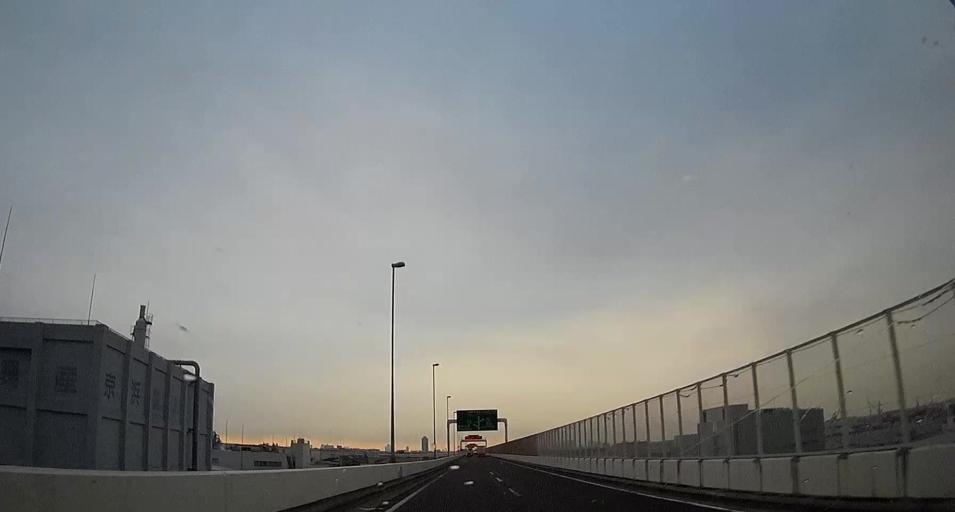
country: JP
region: Kanagawa
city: Yokohama
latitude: 35.4779
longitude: 139.6746
